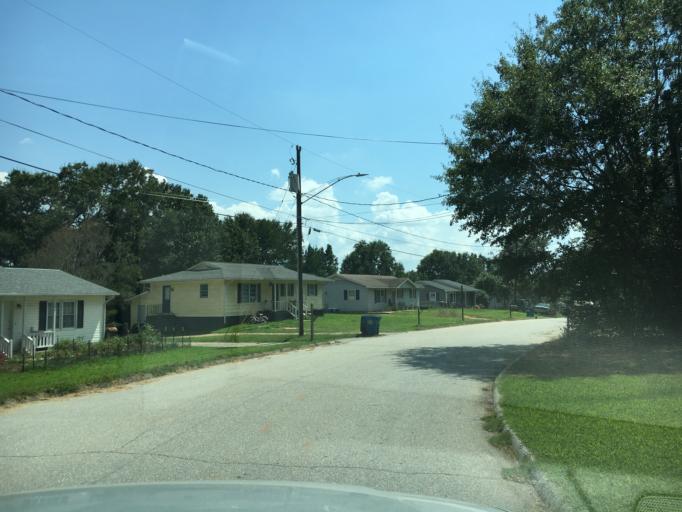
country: US
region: South Carolina
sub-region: Spartanburg County
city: Duncan
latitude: 34.9307
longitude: -82.1351
